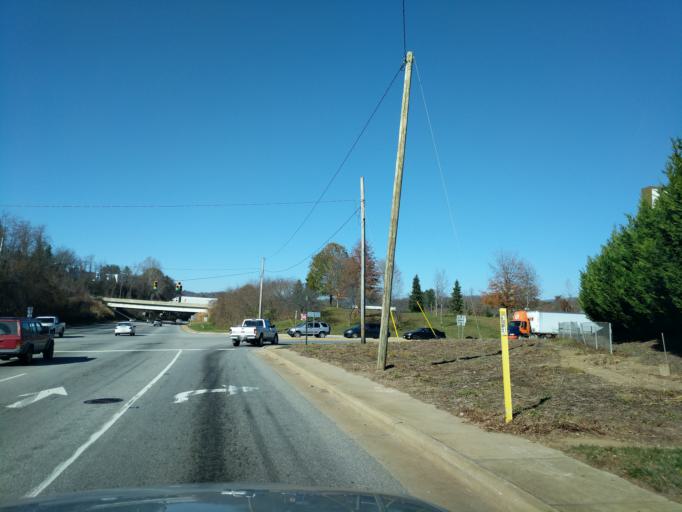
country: US
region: North Carolina
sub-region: Buncombe County
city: Biltmore Forest
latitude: 35.5548
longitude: -82.5203
